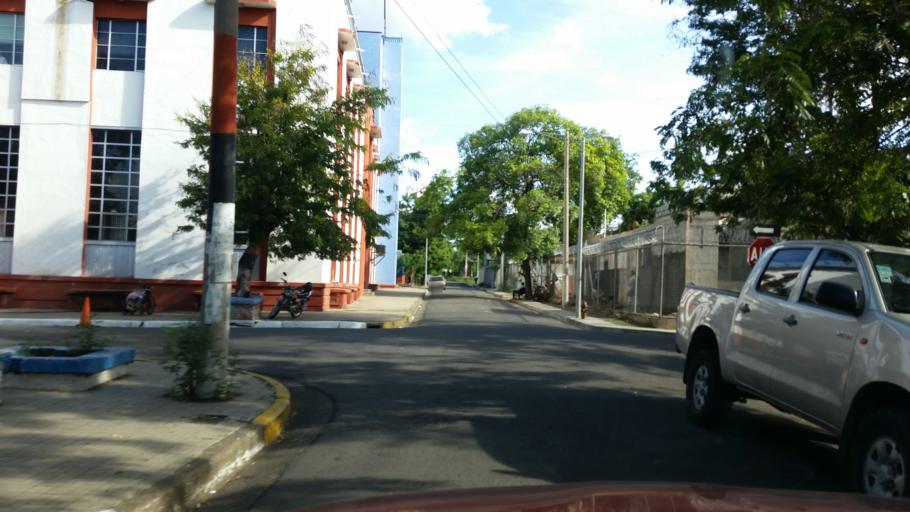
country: NI
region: Managua
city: Managua
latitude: 12.1562
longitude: -86.2748
